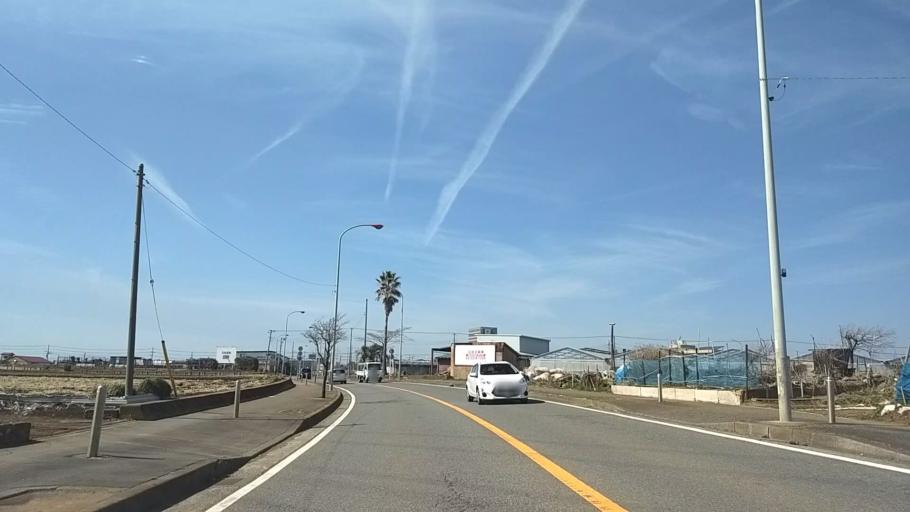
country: JP
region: Kanagawa
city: Fujisawa
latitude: 35.3796
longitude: 139.4805
